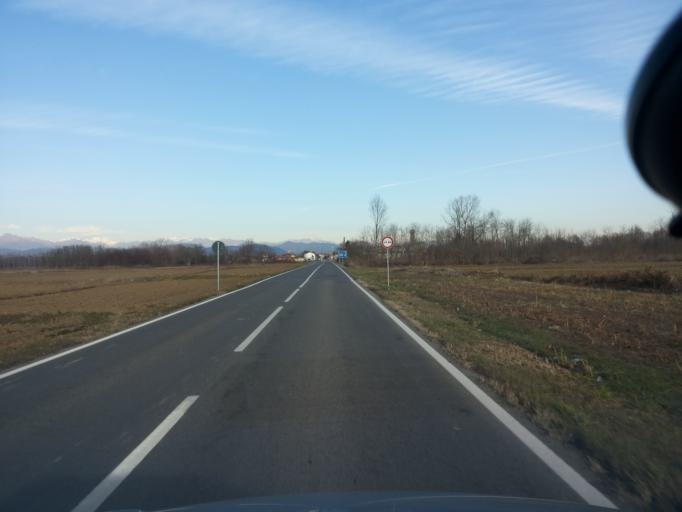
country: IT
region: Piedmont
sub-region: Provincia di Vercelli
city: Lenta
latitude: 45.5453
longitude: 8.3850
